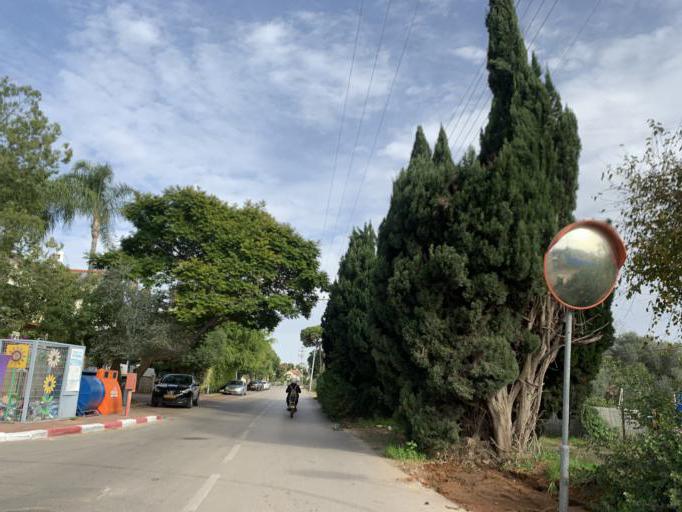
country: IL
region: Central District
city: Hod HaSharon
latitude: 32.1536
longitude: 34.9031
